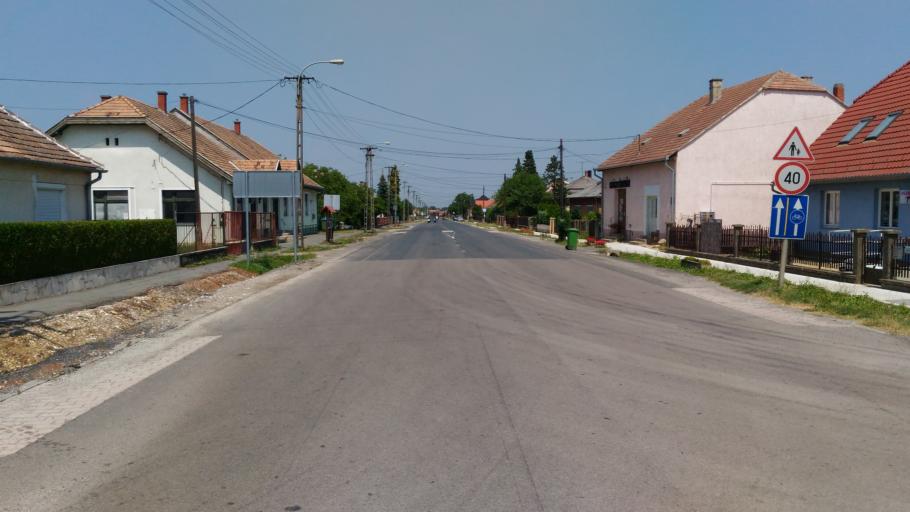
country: HU
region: Vas
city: Kormend
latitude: 46.9664
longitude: 16.6046
